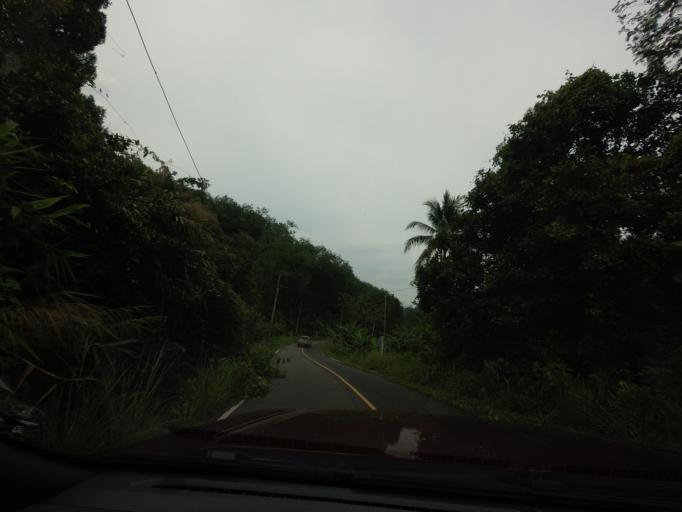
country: TH
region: Narathiwat
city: Si Sakhon
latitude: 6.0633
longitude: 101.3847
